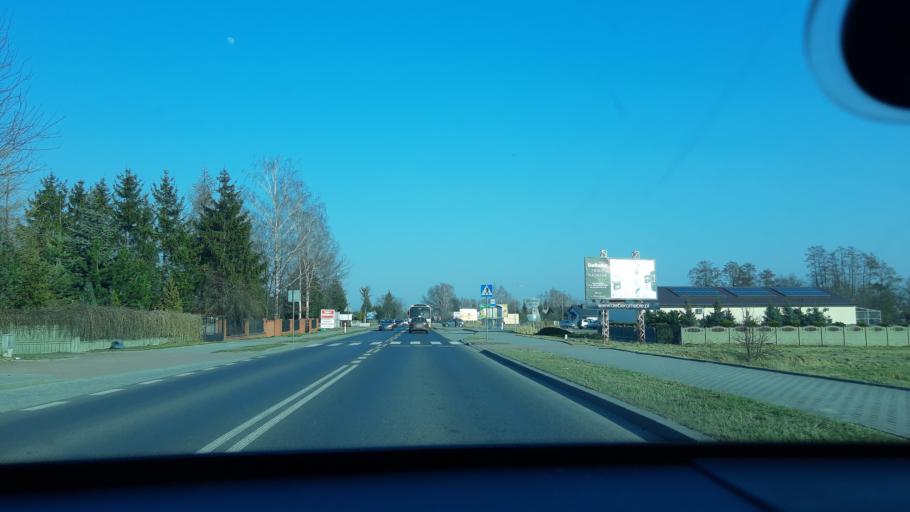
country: PL
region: Lodz Voivodeship
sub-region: Powiat zdunskowolski
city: Zdunska Wola
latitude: 51.6082
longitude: 18.9008
